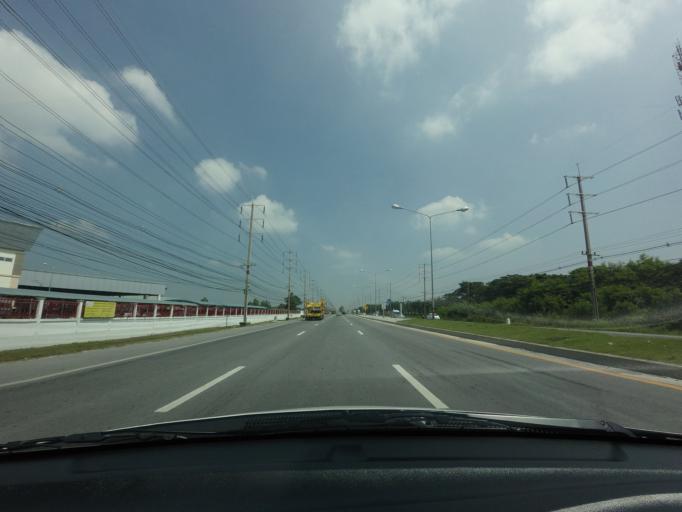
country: TH
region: Chachoengsao
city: Bang Pakong
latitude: 13.5769
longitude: 101.0050
